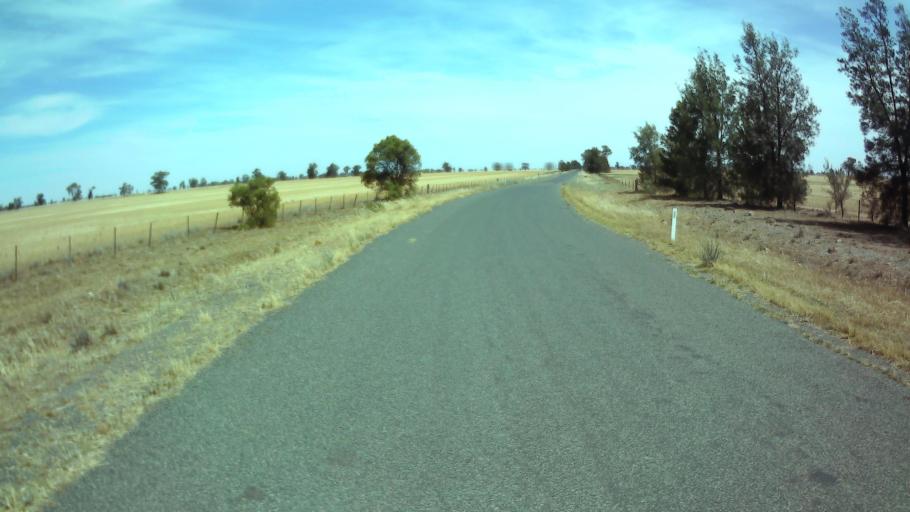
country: AU
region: New South Wales
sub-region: Weddin
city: Grenfell
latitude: -33.9119
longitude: 147.7655
